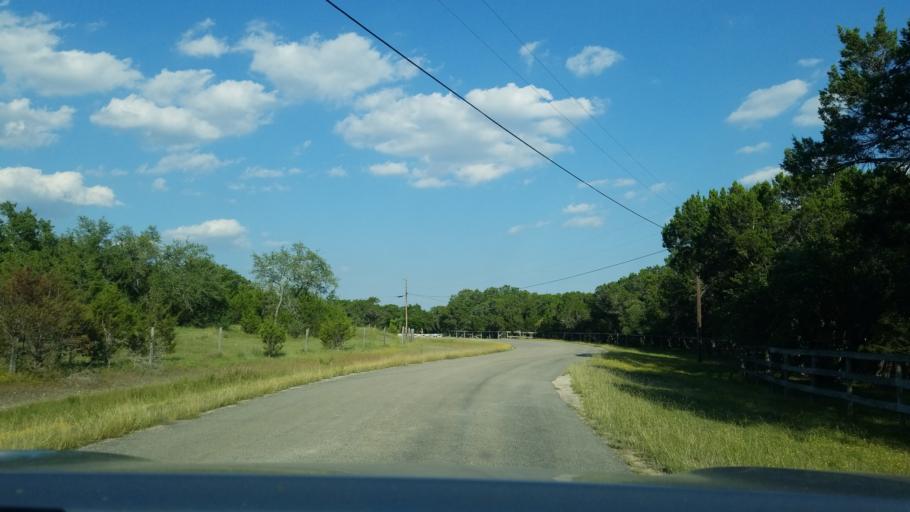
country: US
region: Texas
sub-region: Comal County
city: Bulverde
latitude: 29.7893
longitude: -98.4277
